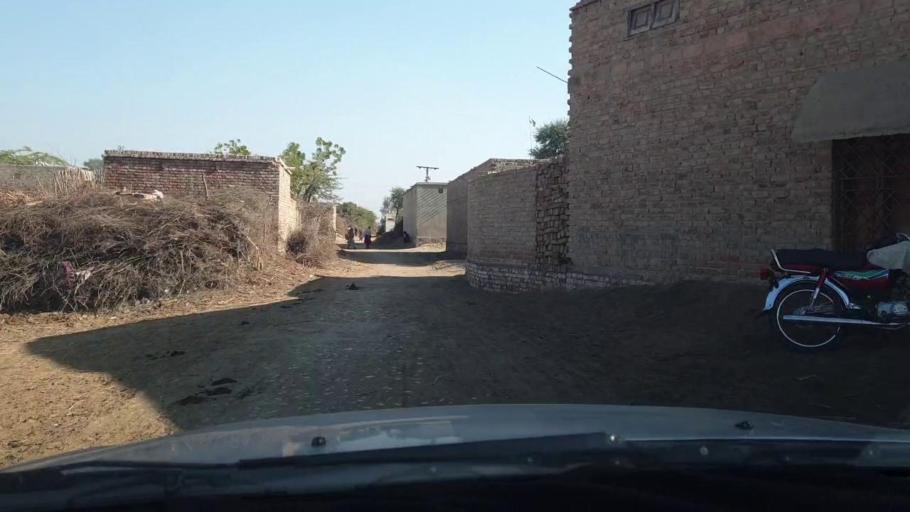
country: PK
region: Sindh
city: Mirpur Mathelo
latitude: 27.9757
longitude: 69.5496
